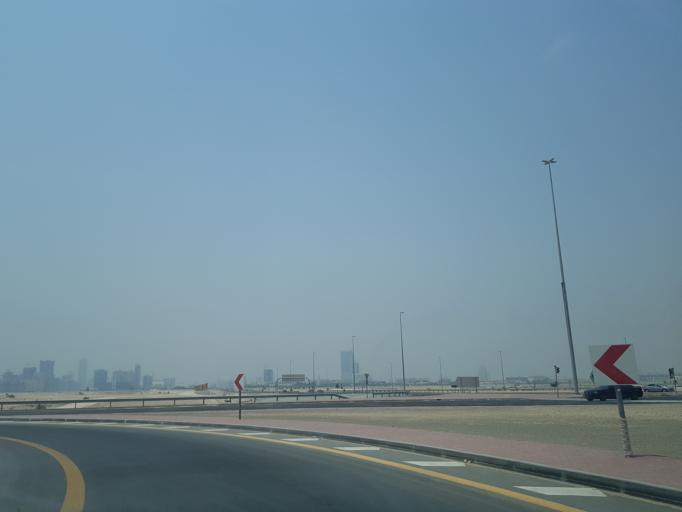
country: AE
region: Dubai
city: Dubai
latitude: 25.0238
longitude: 55.2388
